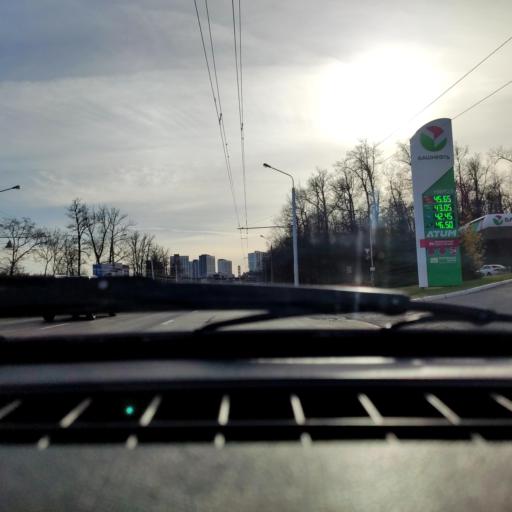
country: RU
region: Bashkortostan
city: Ufa
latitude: 54.7314
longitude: 56.0248
